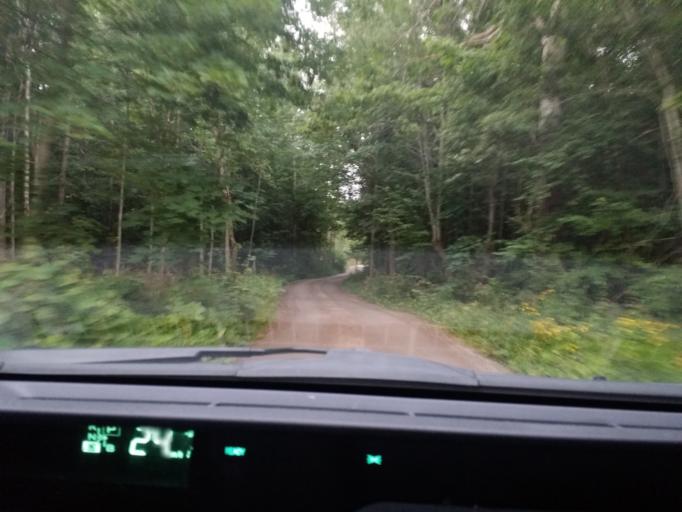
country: SE
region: Kalmar
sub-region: Borgholms Kommun
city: Borgholm
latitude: 57.2093
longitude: 16.9569
